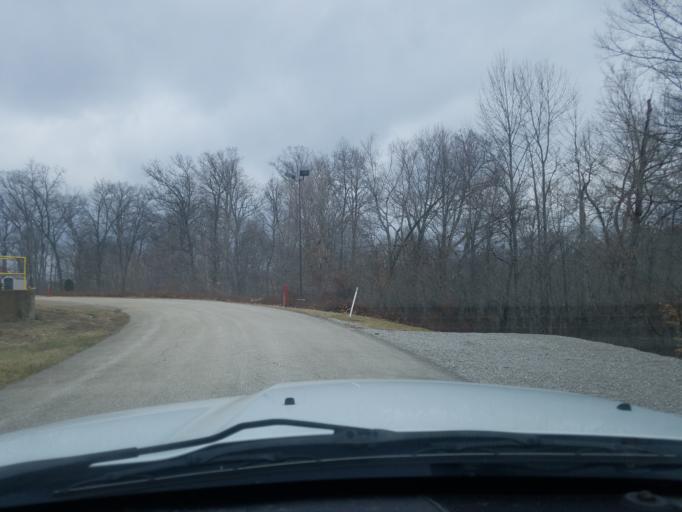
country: US
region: Indiana
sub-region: Perry County
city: Tell City
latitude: 37.9908
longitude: -86.7146
